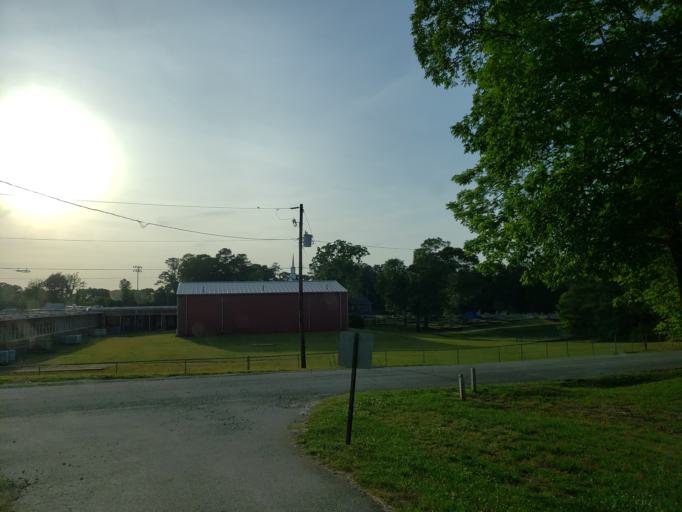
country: US
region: Georgia
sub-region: Carroll County
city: Mount Zion
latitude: 33.6348
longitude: -85.1855
